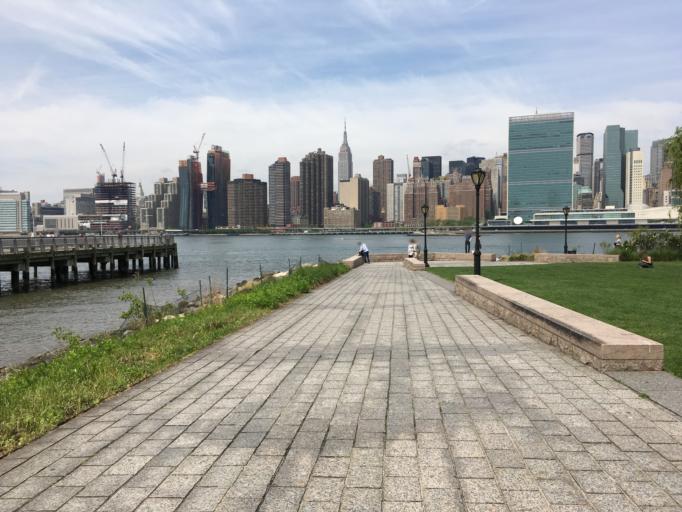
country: US
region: New York
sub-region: Queens County
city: Long Island City
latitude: 40.7453
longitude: -73.9587
